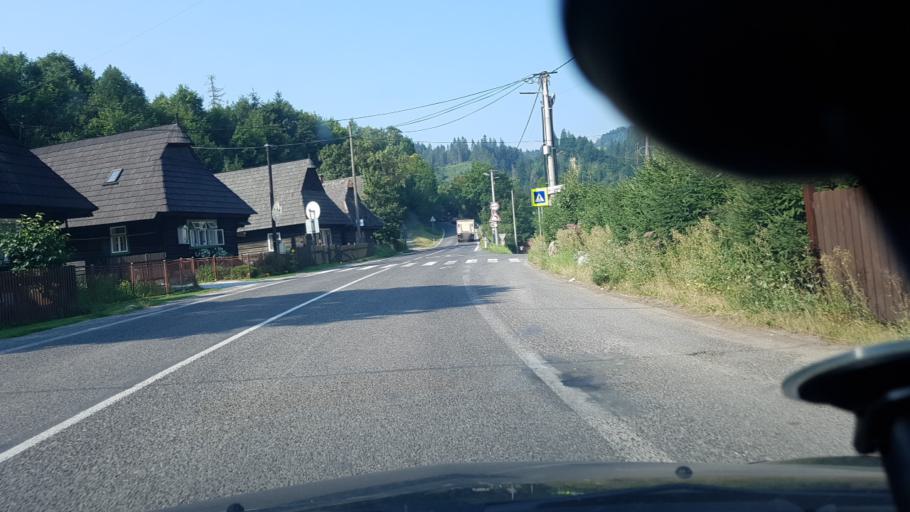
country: SK
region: Zilinsky
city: Tvrdosin
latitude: 49.3059
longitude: 19.4831
